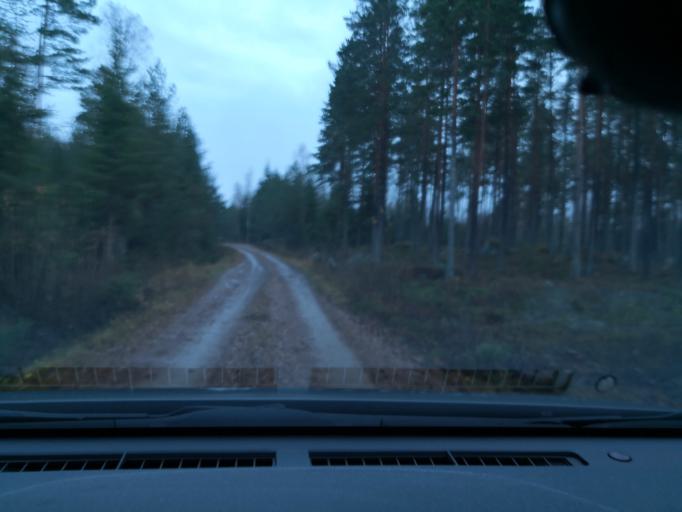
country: SE
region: Vaestmanland
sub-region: Hallstahammars Kommun
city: Kolback
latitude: 59.5513
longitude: 16.1671
